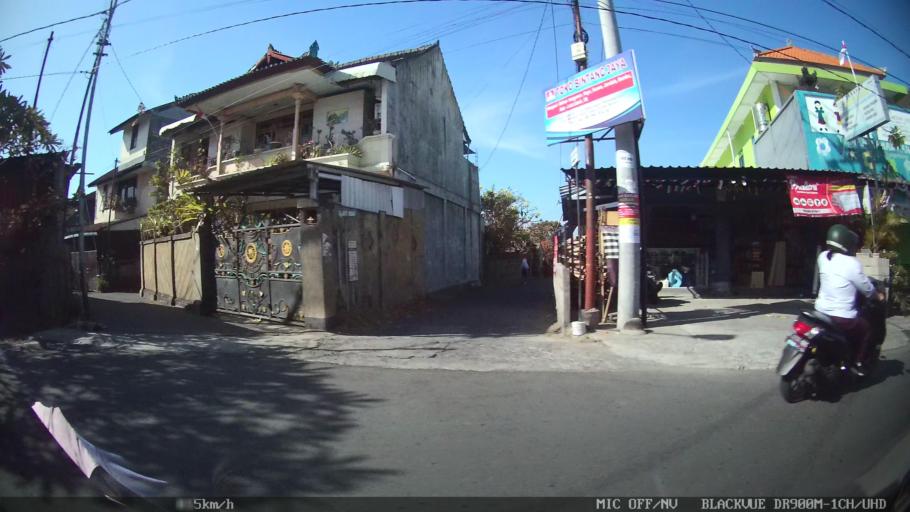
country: ID
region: Bali
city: Banjar Karangsuling
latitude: -8.6189
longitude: 115.1833
